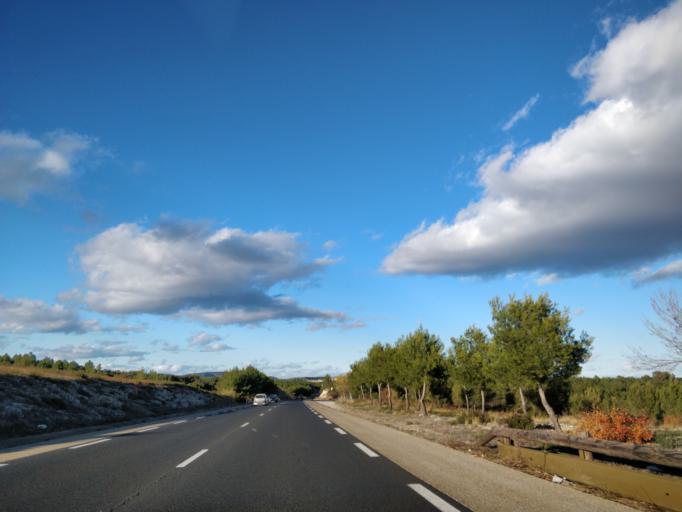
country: FR
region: Languedoc-Roussillon
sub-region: Departement de l'Herault
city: Teyran
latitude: 43.6919
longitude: 3.9434
